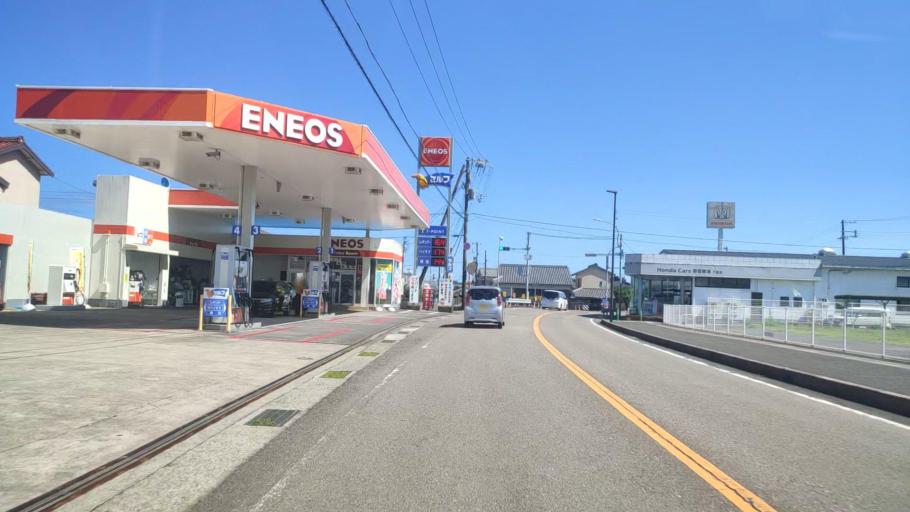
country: JP
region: Wakayama
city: Shingu
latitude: 33.5827
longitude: 135.9201
